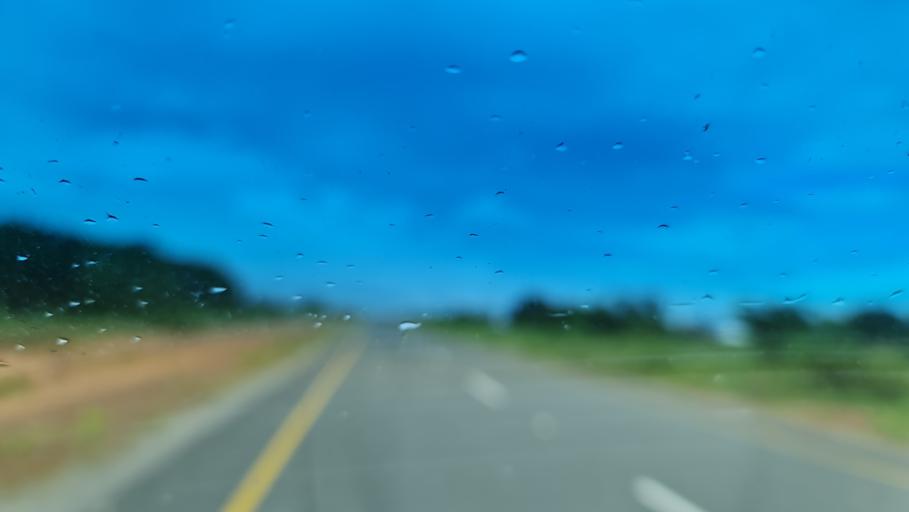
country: MZ
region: Nampula
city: Nampula
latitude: -15.5526
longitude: 39.3220
